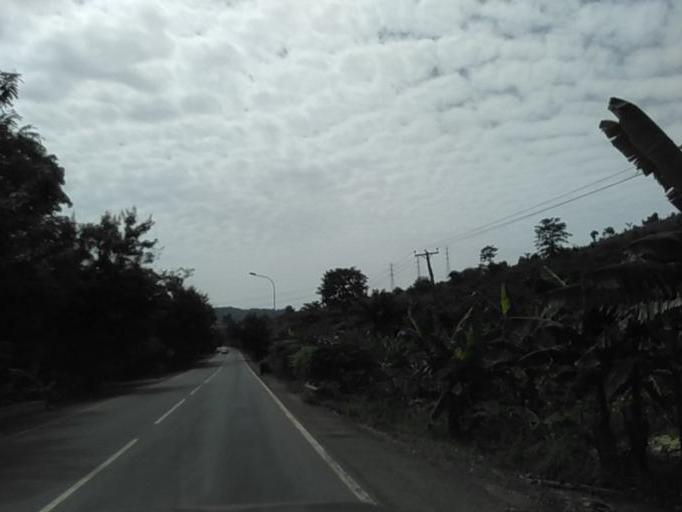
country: GH
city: Akropong
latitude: 6.2670
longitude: 0.0686
